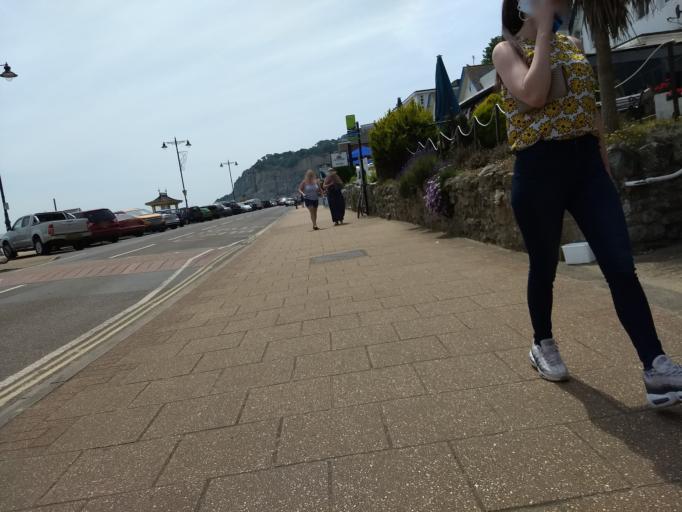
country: GB
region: England
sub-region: Isle of Wight
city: Shanklin
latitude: 50.6291
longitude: -1.1726
